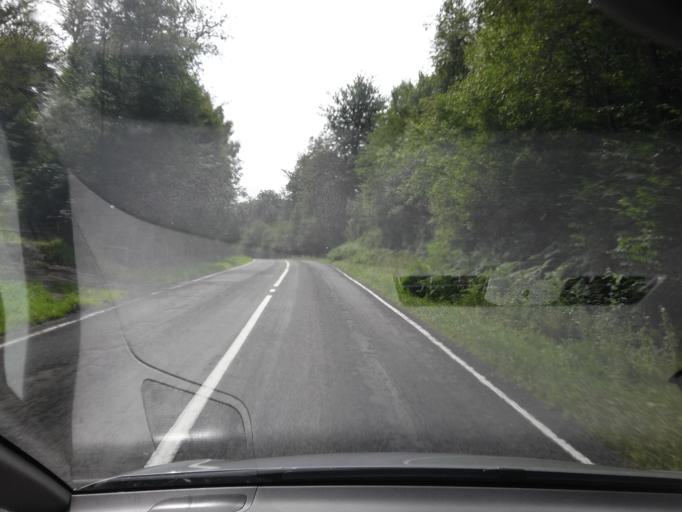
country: BE
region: Wallonia
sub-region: Province du Luxembourg
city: Chiny
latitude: 49.7766
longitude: 5.3500
